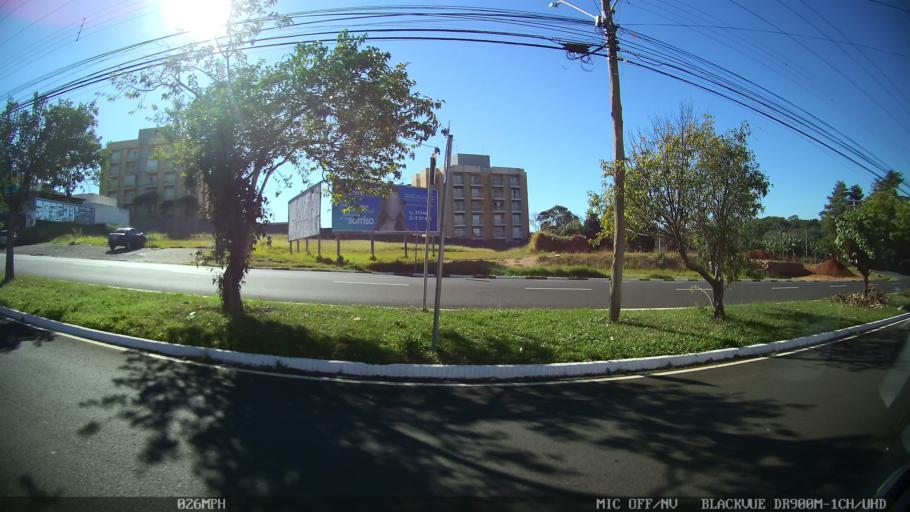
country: BR
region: Sao Paulo
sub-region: Franca
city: Franca
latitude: -20.5524
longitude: -47.3868
